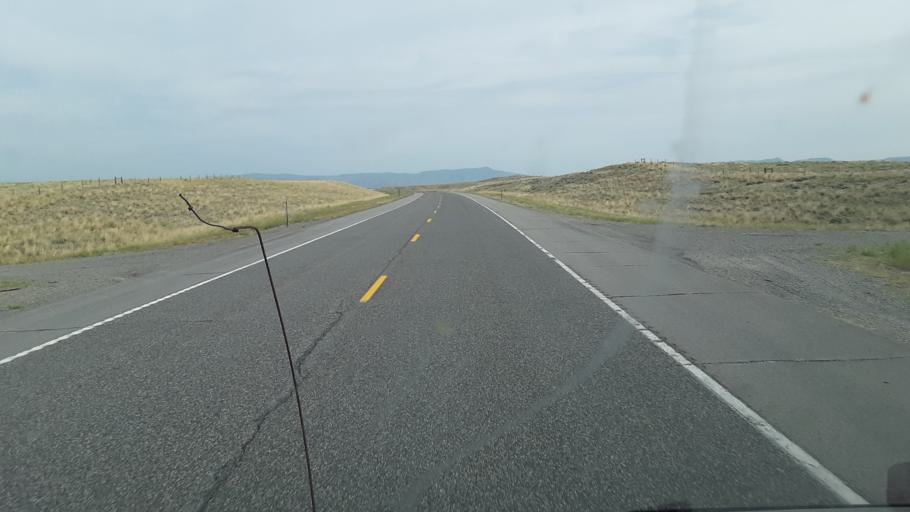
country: US
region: Wyoming
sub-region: Fremont County
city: Riverton
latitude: 43.2659
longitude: -108.1127
